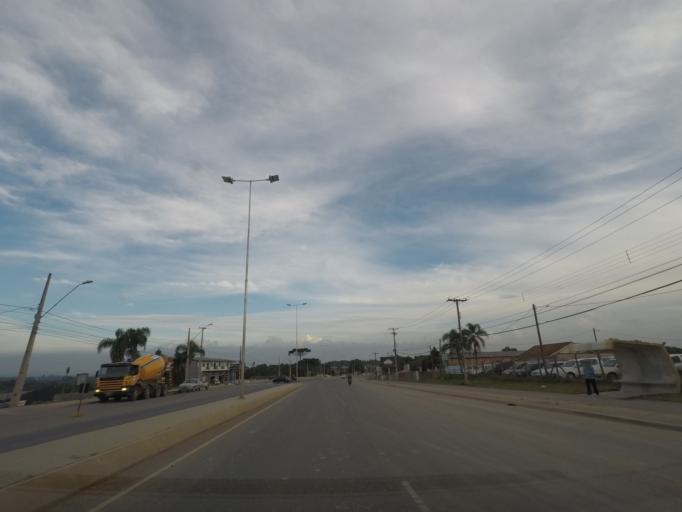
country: BR
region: Parana
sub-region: Colombo
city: Colombo
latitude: -25.3091
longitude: -49.2217
